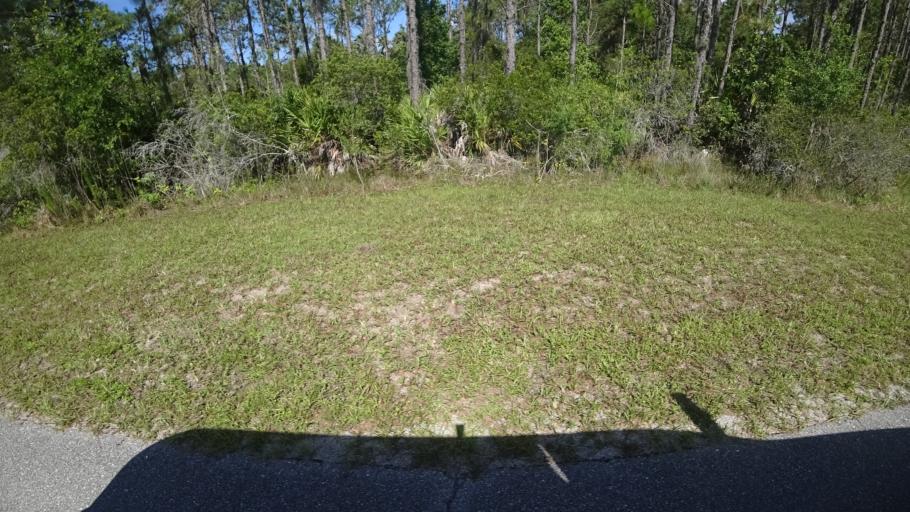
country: US
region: Florida
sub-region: Sarasota County
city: The Meadows
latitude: 27.4212
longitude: -82.3182
